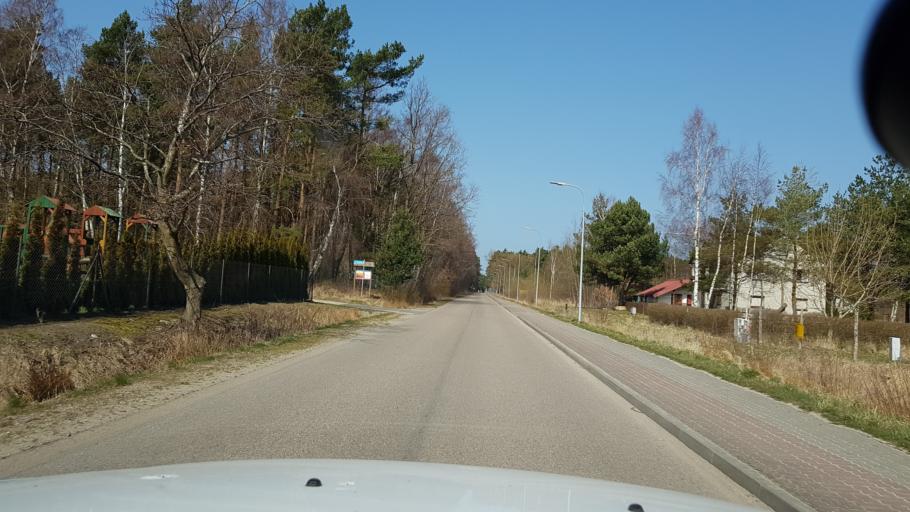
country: PL
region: West Pomeranian Voivodeship
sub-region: Powiat slawienski
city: Darlowo
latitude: 54.5196
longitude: 16.5135
